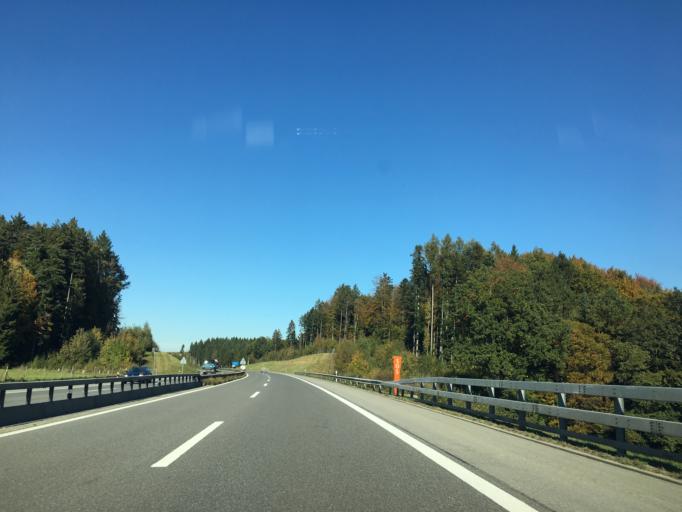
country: CH
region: Fribourg
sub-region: Gruyere District
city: La Roche
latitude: 46.7086
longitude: 7.0907
